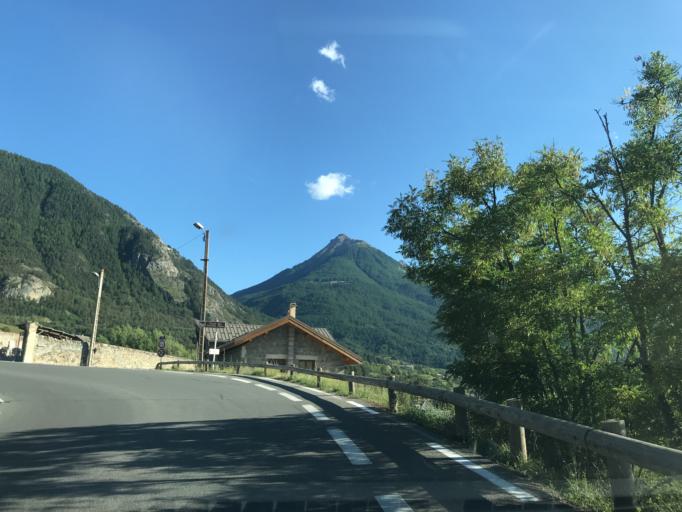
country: FR
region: Provence-Alpes-Cote d'Azur
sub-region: Departement des Hautes-Alpes
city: Briancon
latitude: 44.8892
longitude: 6.6393
